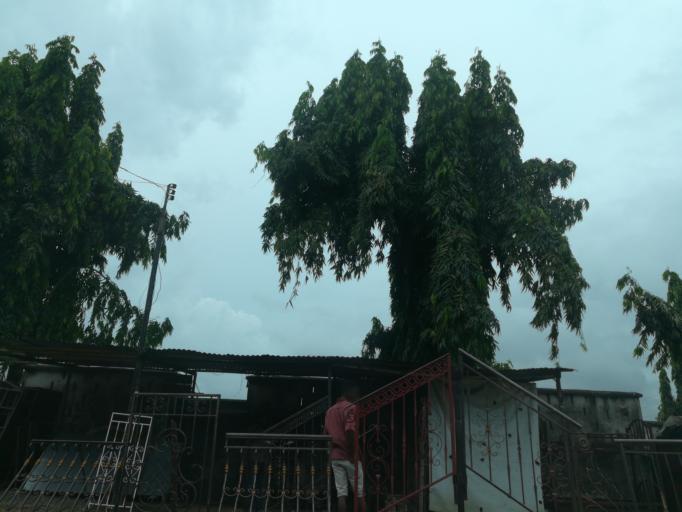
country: NG
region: Rivers
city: Port Harcourt
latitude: 4.8340
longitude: 7.0301
